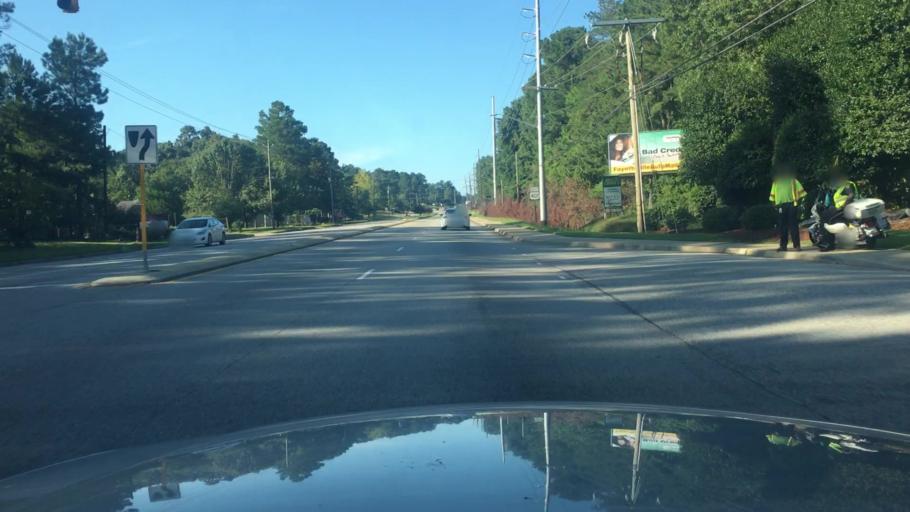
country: US
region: North Carolina
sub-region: Cumberland County
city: Eastover
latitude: 35.1484
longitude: -78.8713
